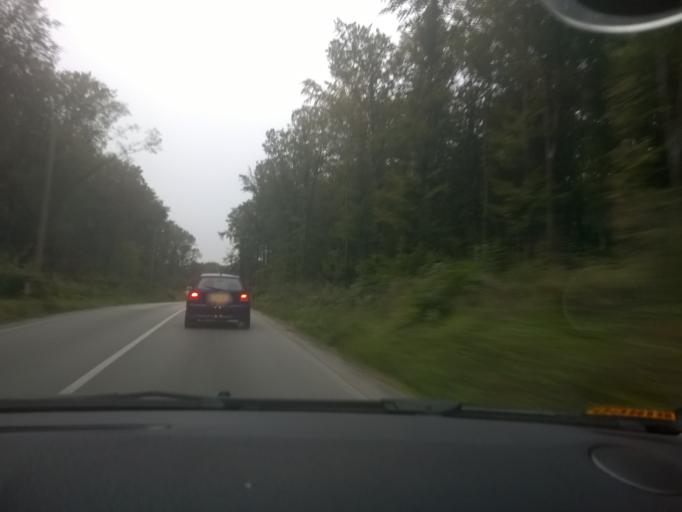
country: HR
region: Zagrebacka
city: Pojatno
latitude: 45.8942
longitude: 15.7950
